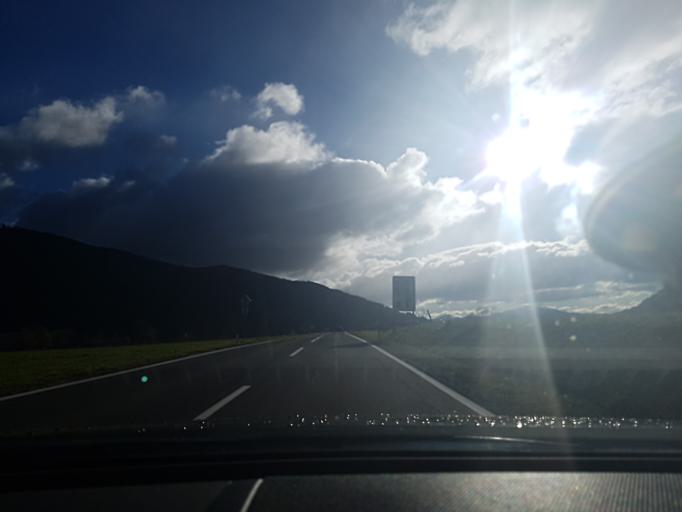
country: AT
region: Styria
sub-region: Politischer Bezirk Murtal
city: Oberzeiring
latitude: 47.2601
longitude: 14.5001
